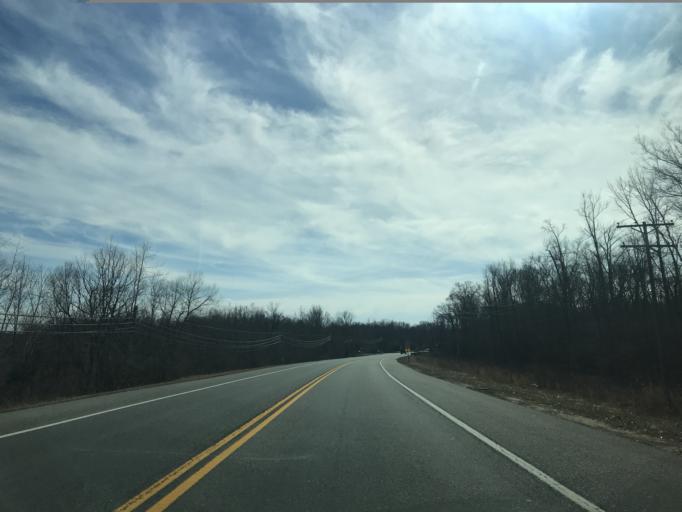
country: US
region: Maryland
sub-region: Charles County
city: Potomac Heights
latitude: 38.5925
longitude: -77.1204
